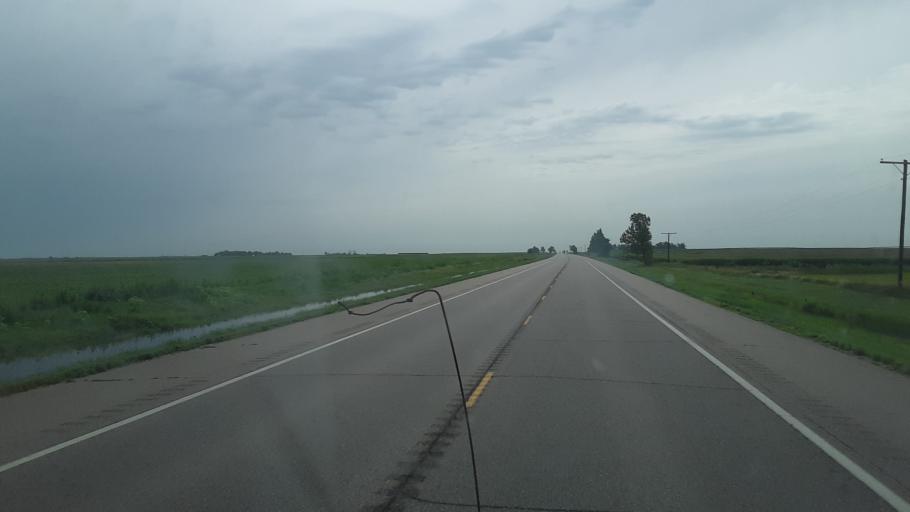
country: US
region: Kansas
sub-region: Stafford County
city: Saint John
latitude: 37.9564
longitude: -98.9479
